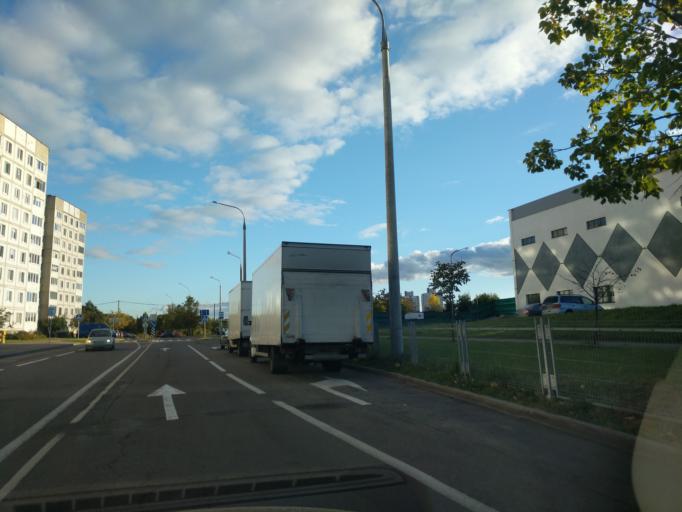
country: BY
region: Minsk
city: Malinovka
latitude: 53.8630
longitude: 27.4485
